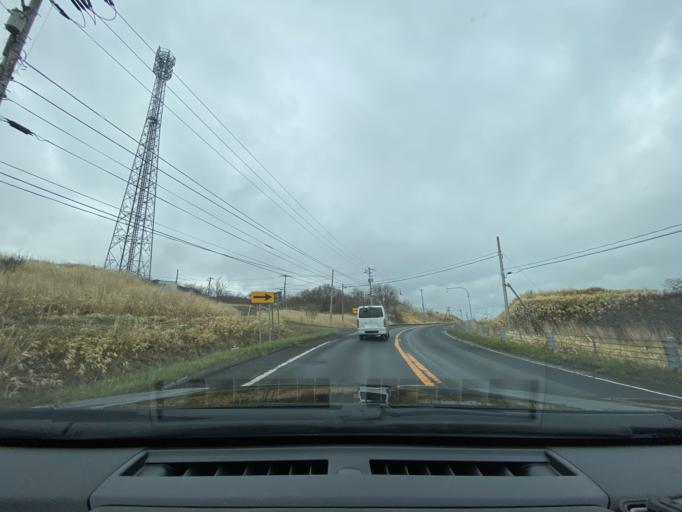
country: JP
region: Hokkaido
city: Ishikari
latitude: 43.3907
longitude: 141.4336
